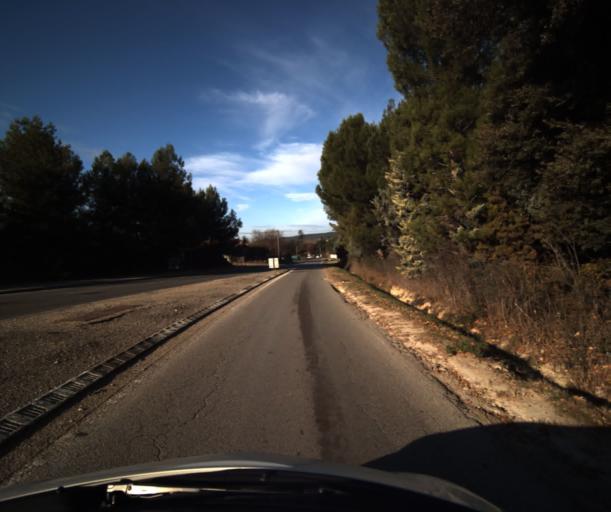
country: FR
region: Provence-Alpes-Cote d'Azur
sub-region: Departement du Vaucluse
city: Pertuis
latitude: 43.6961
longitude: 5.5216
